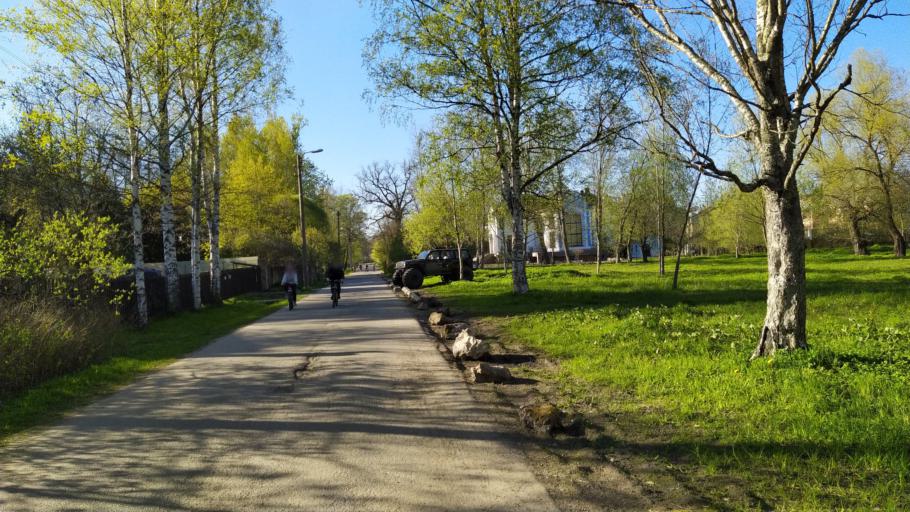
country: RU
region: St.-Petersburg
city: Tyarlevo
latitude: 59.6792
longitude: 30.4612
